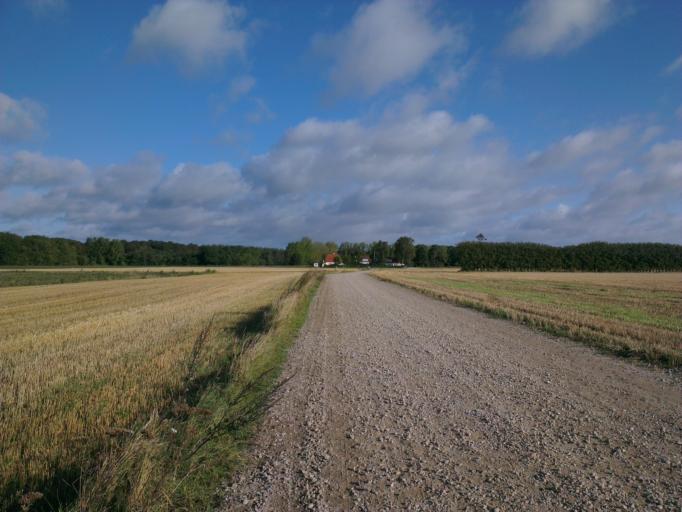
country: DK
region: Capital Region
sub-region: Frederikssund Kommune
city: Jaegerspris
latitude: 55.8654
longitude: 11.9949
